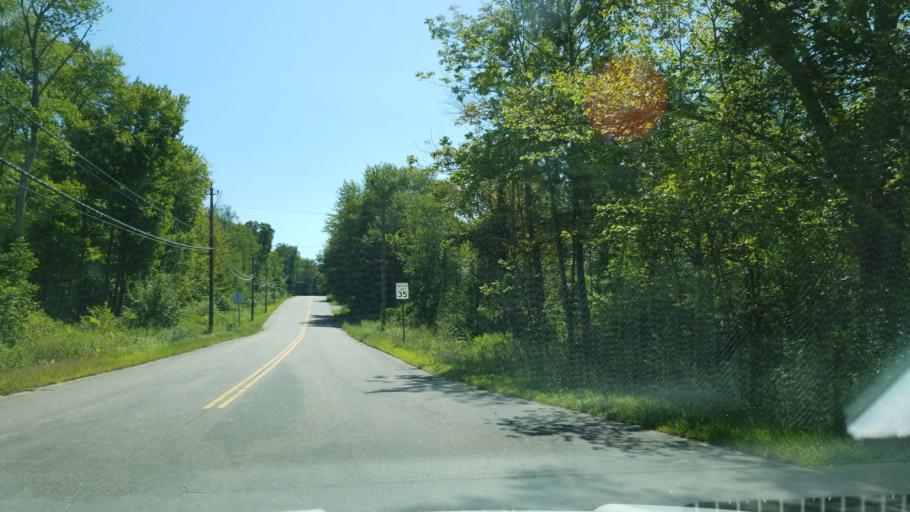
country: US
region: Connecticut
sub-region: Hartford County
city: Tariffville
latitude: 41.8514
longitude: -72.7524
